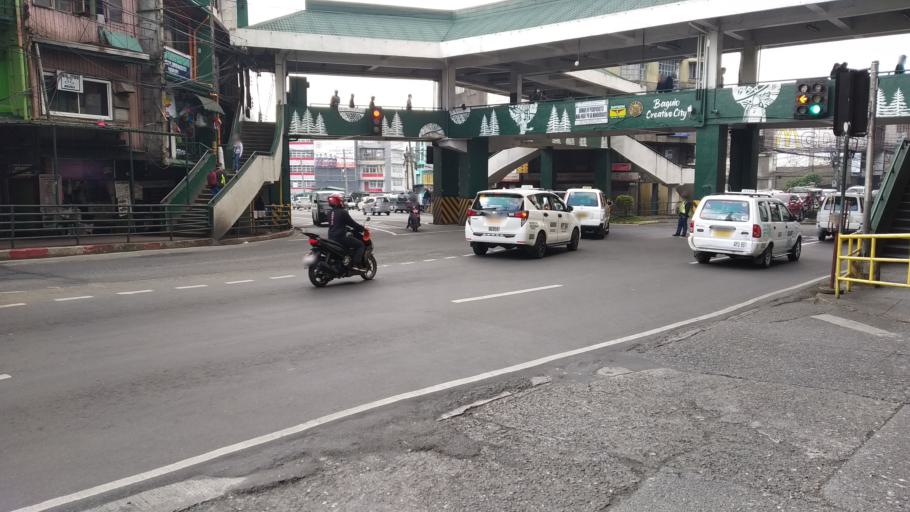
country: PH
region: Cordillera
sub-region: Baguio City
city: Baguio
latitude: 16.4166
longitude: 120.5961
